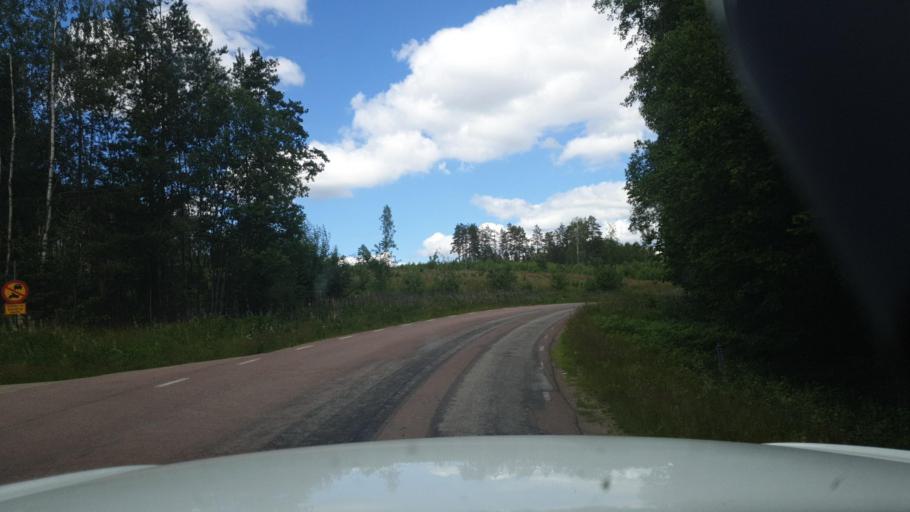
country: SE
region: Vaermland
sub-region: Arvika Kommun
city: Arvika
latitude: 59.6736
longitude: 12.4700
